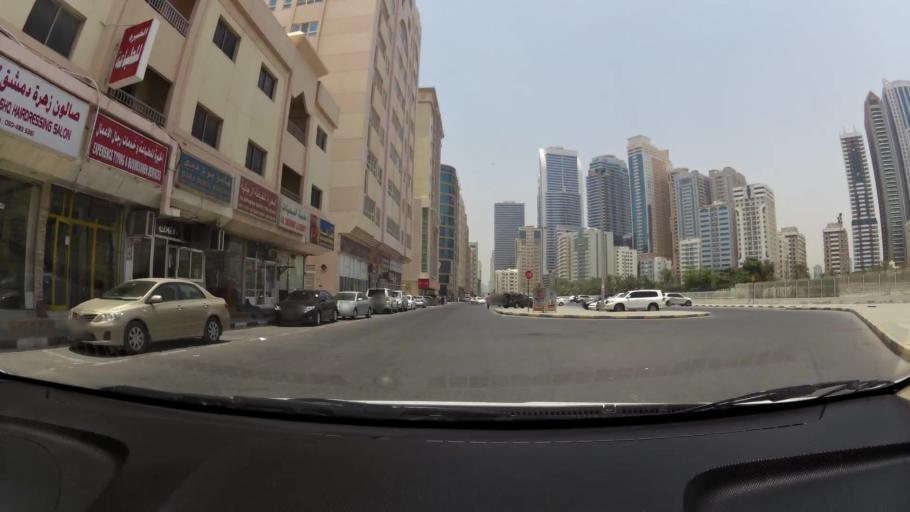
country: AE
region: Ash Shariqah
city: Sharjah
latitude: 25.3321
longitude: 55.3716
